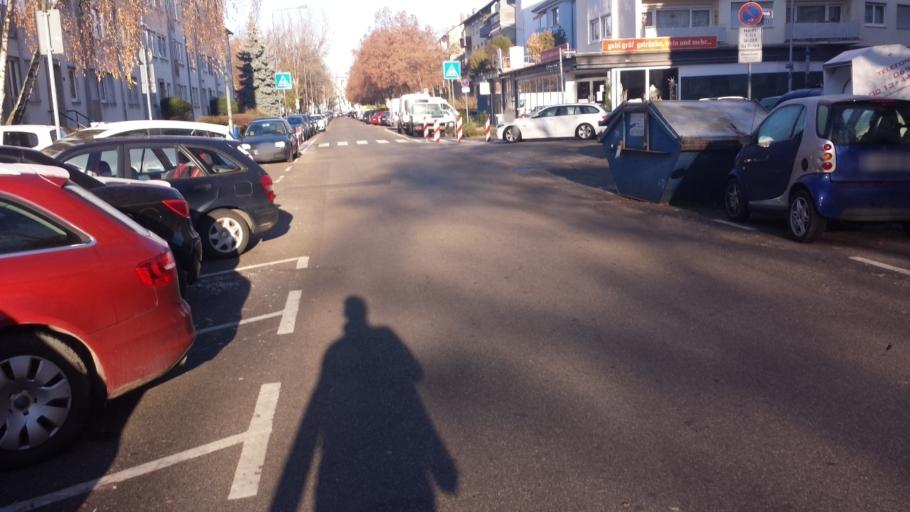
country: DE
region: Hesse
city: Niederrad
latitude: 50.0788
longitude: 8.6475
